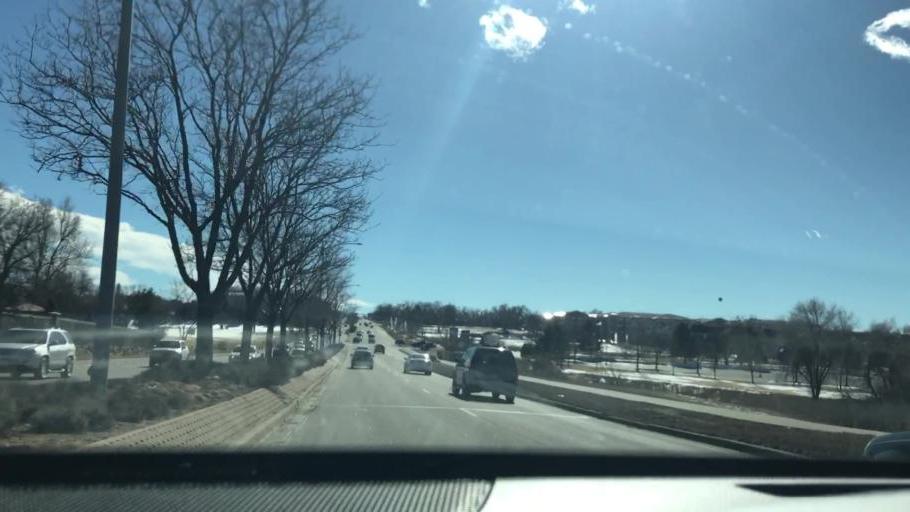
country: US
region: Colorado
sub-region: Adams County
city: Westminster
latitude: 39.8763
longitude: -105.0532
